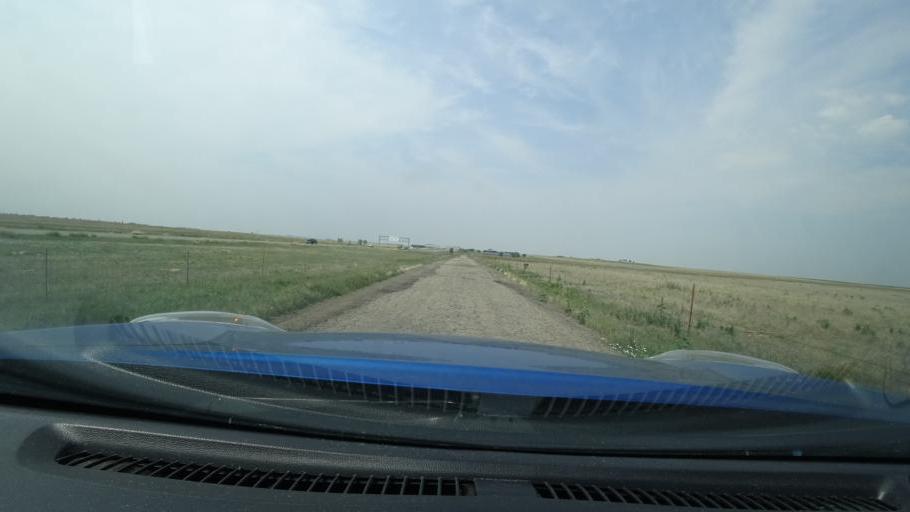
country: US
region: Colorado
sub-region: Adams County
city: Aurora
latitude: 39.7616
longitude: -104.7158
